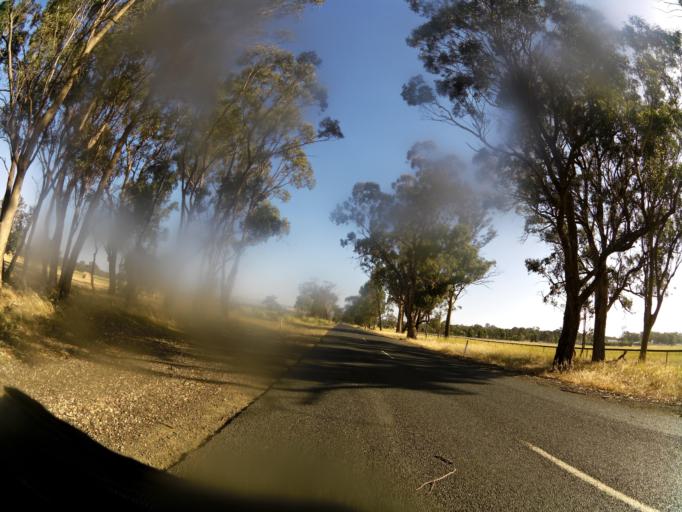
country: AU
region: Victoria
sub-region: Murrindindi
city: Kinglake West
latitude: -36.9811
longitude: 145.1108
